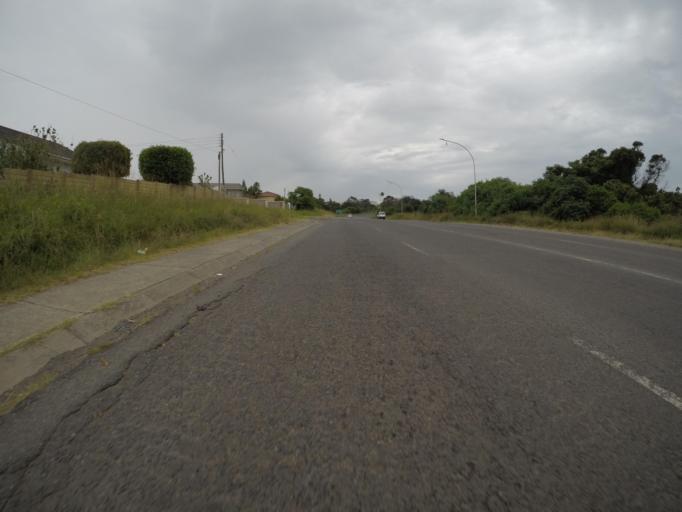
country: ZA
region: Eastern Cape
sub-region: Buffalo City Metropolitan Municipality
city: East London
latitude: -32.9913
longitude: 27.8588
